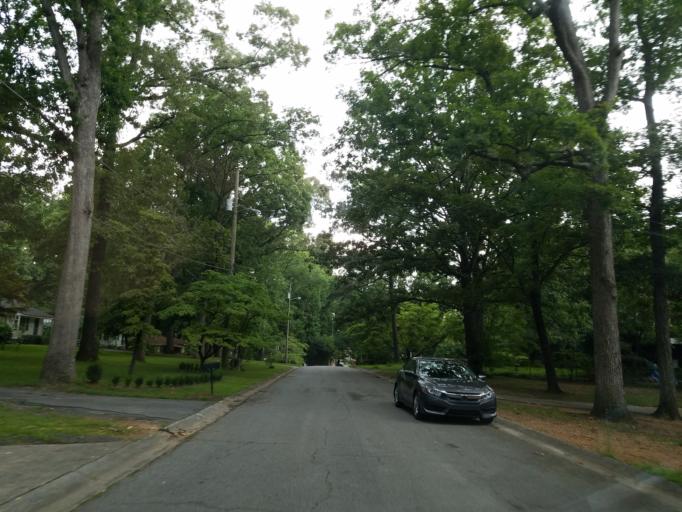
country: US
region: Georgia
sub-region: Cobb County
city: Marietta
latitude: 33.9390
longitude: -84.5492
